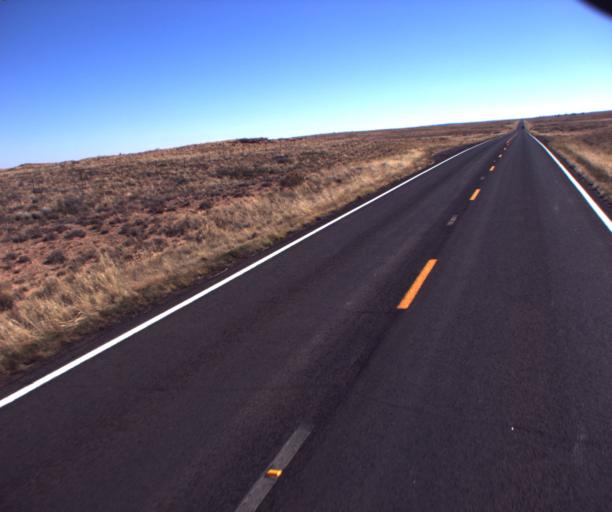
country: US
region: Arizona
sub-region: Coconino County
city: Tuba City
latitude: 35.9699
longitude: -110.9615
